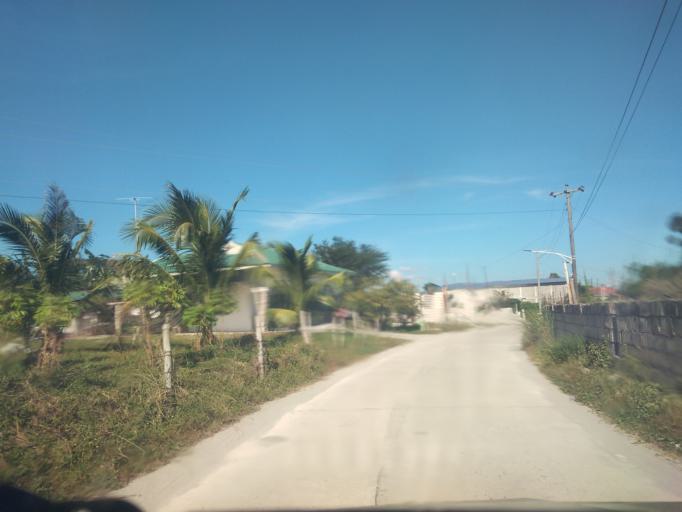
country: PH
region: Central Luzon
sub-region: Province of Pampanga
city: Calibutbut
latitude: 15.0926
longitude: 120.5934
